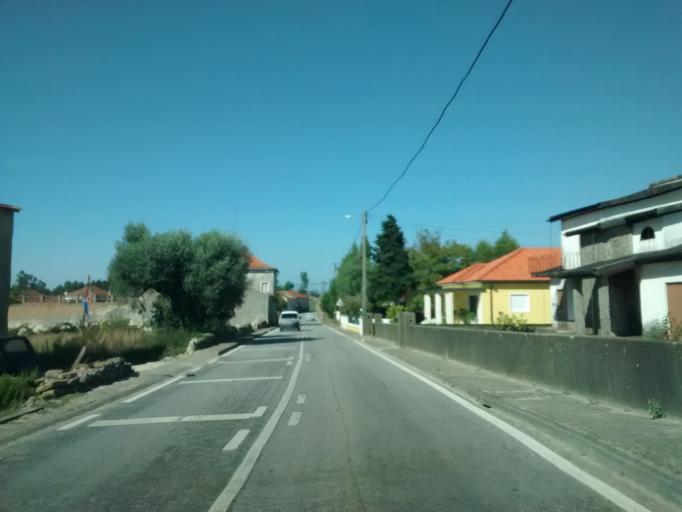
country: PT
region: Aveiro
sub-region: Anadia
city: Sangalhos
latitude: 40.4317
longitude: -8.5115
